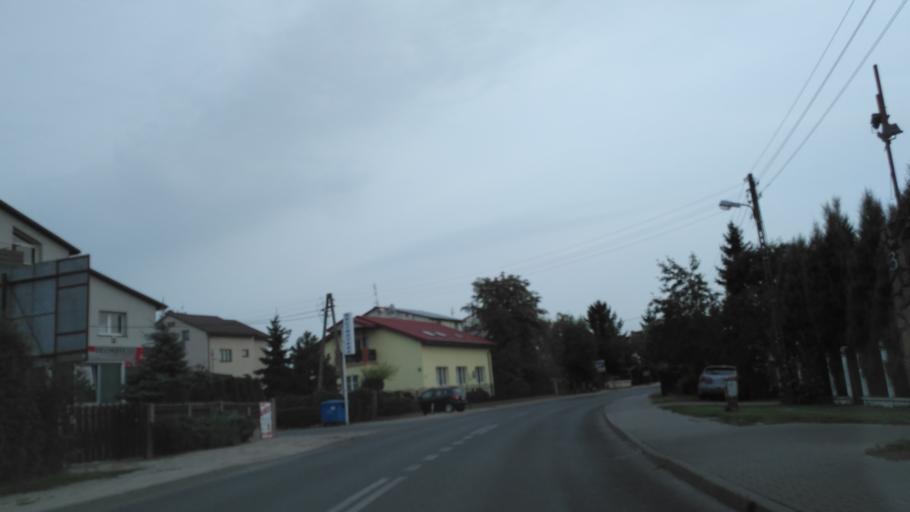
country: PL
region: Lublin Voivodeship
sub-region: Powiat lubelski
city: Lublin
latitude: 51.2241
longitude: 22.5876
